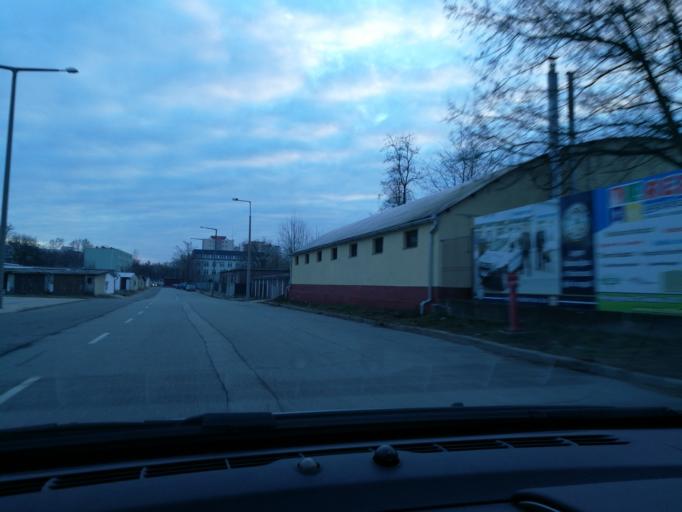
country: HU
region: Szabolcs-Szatmar-Bereg
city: Nyiregyhaza
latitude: 47.9710
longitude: 21.7114
